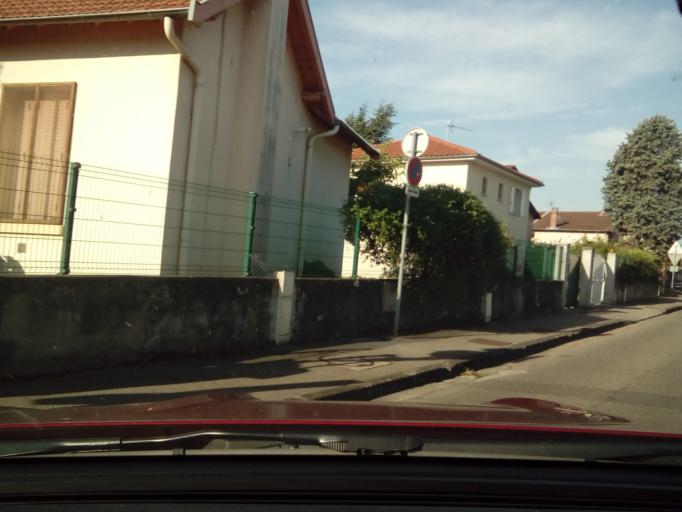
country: FR
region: Rhone-Alpes
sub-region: Departement du Rhone
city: Bron
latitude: 45.7391
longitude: 4.9102
